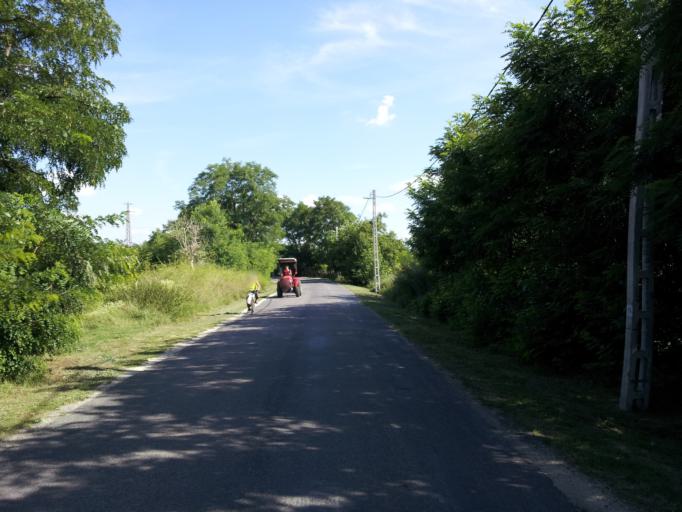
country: HU
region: Pest
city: Kiskunlachaza
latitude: 47.2168
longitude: 19.0151
